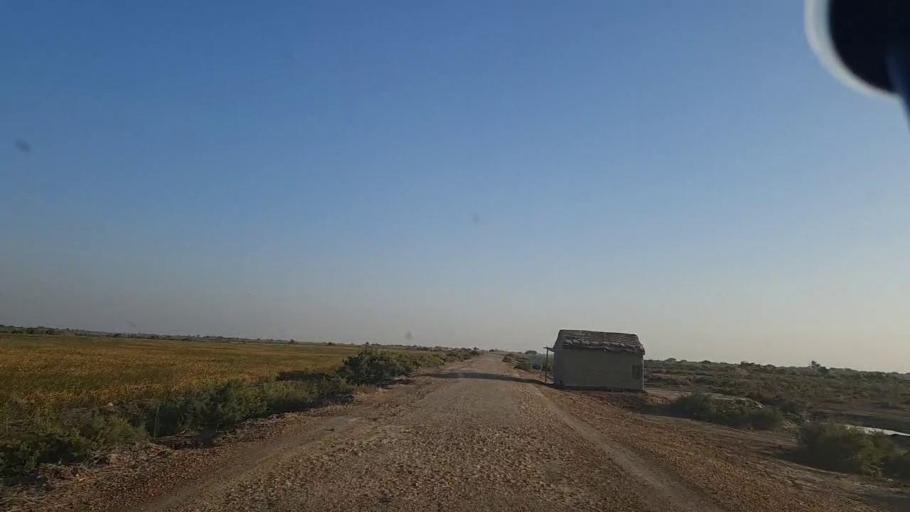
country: PK
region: Sindh
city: Chuhar Jamali
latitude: 24.4719
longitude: 68.0919
